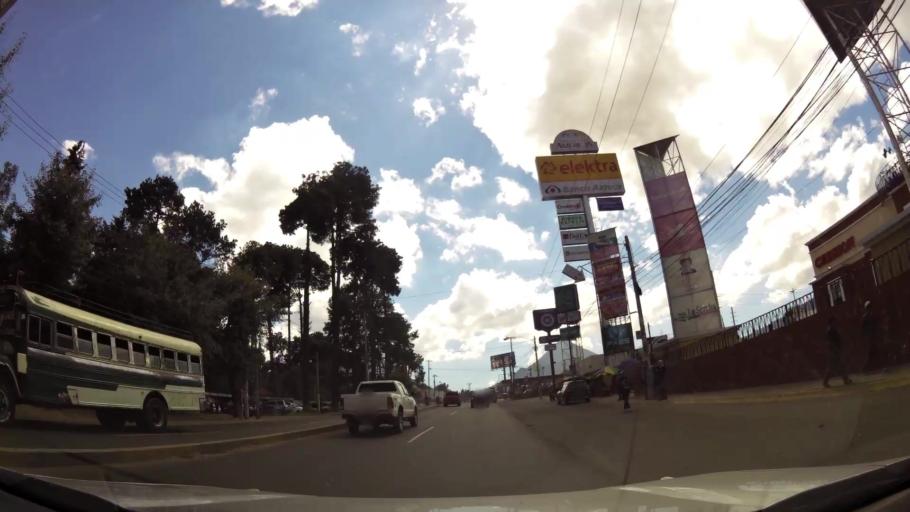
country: GT
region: Quetzaltenango
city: Quetzaltenango
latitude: 14.8480
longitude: -91.5367
